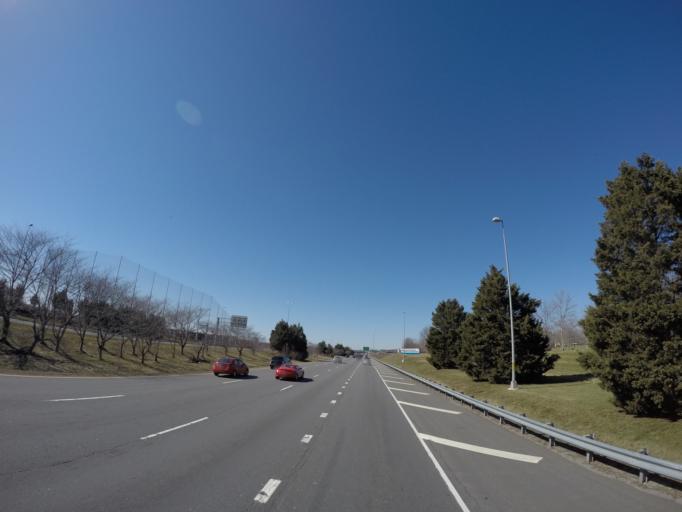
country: US
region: Virginia
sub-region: Loudoun County
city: University Center
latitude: 39.0525
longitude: -77.4423
